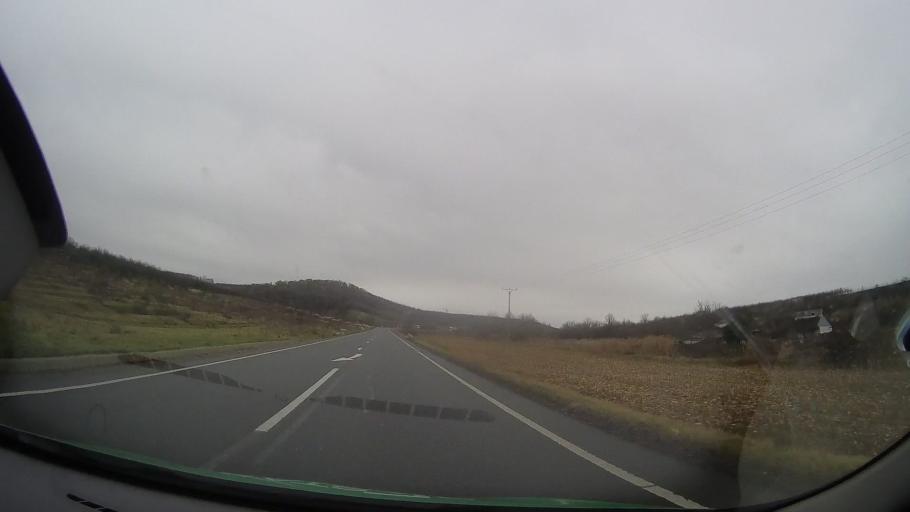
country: RO
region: Mures
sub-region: Comuna Breaza
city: Breaza
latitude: 46.7826
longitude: 24.6526
